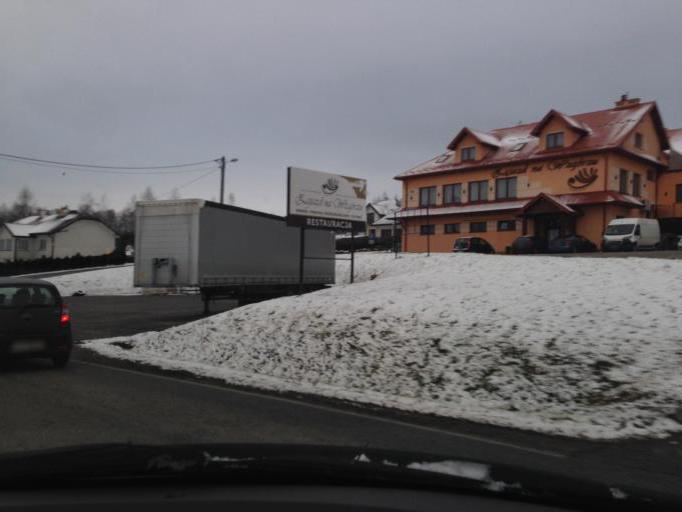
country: PL
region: Lesser Poland Voivodeship
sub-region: Powiat gorlicki
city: Moszczenica
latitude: 49.7424
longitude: 21.0831
